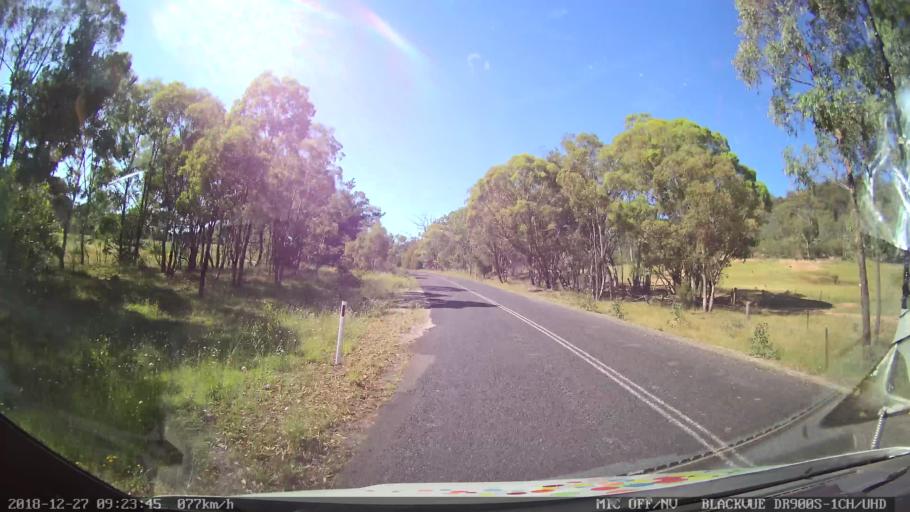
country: AU
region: New South Wales
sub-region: Lithgow
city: Portland
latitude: -33.1292
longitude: 149.9957
